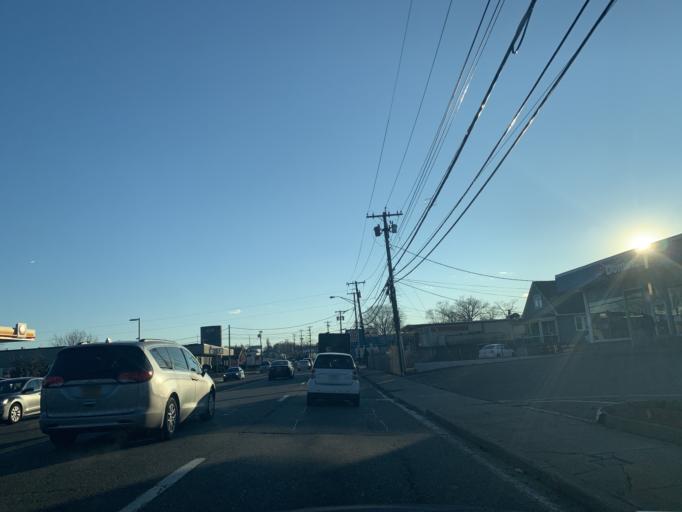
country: US
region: Rhode Island
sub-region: Providence County
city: East Providence
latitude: 41.8163
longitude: -71.3570
